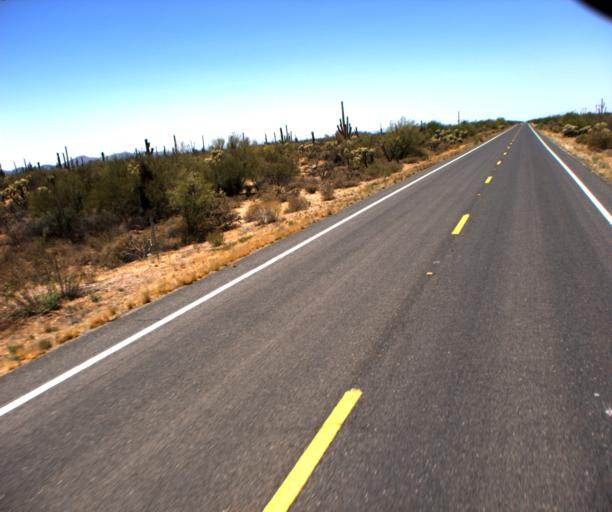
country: US
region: Arizona
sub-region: Pinal County
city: Florence
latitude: 32.8167
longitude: -111.1984
